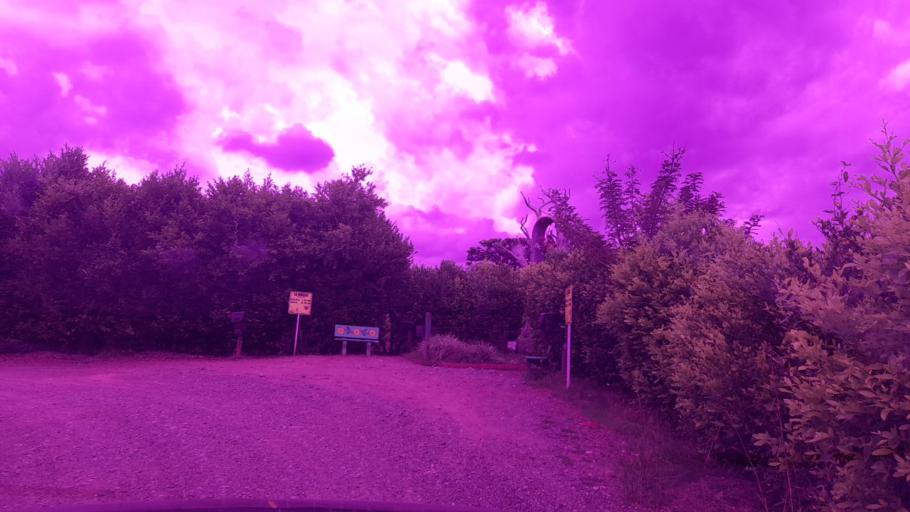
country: CO
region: Valle del Cauca
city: Andalucia
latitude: 4.1695
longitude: -76.1188
